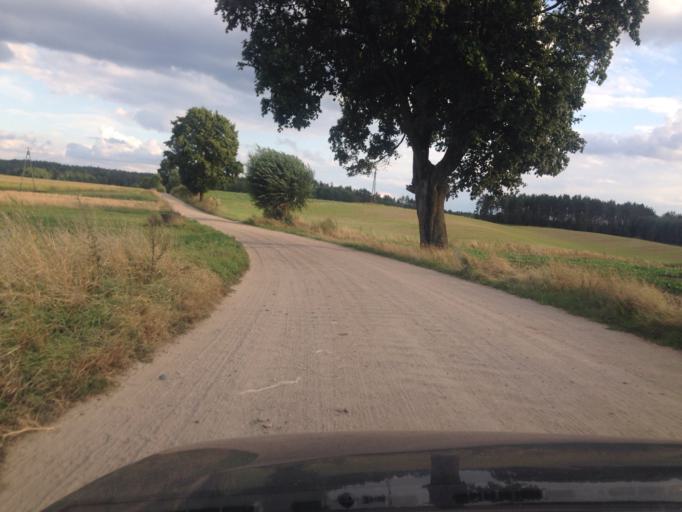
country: PL
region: Kujawsko-Pomorskie
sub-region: Powiat brodnicki
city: Bartniczka
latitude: 53.2821
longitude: 19.6985
